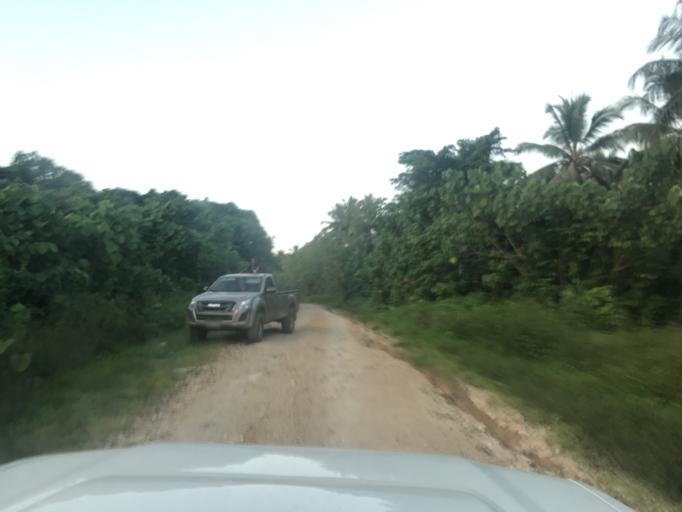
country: VU
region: Sanma
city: Luganville
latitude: -15.5561
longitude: 166.9680
